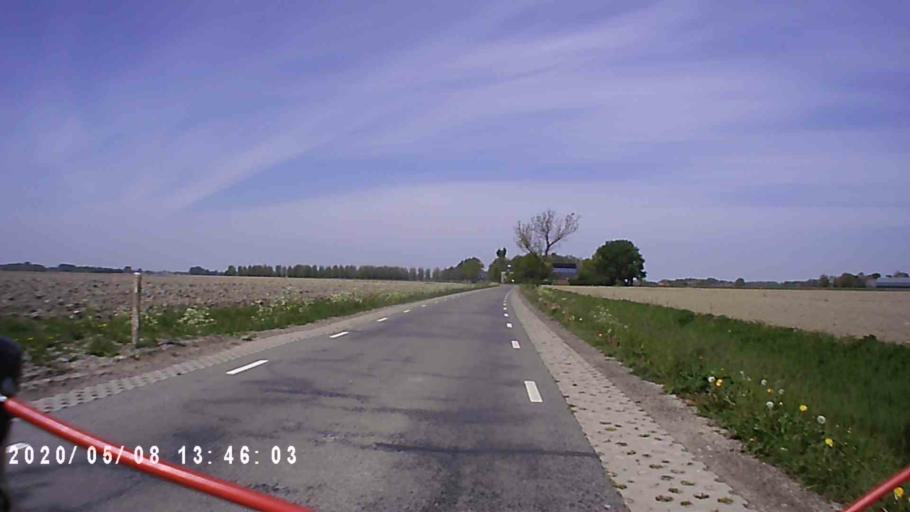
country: NL
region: Groningen
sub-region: Gemeente Appingedam
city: Appingedam
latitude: 53.3287
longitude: 6.7876
